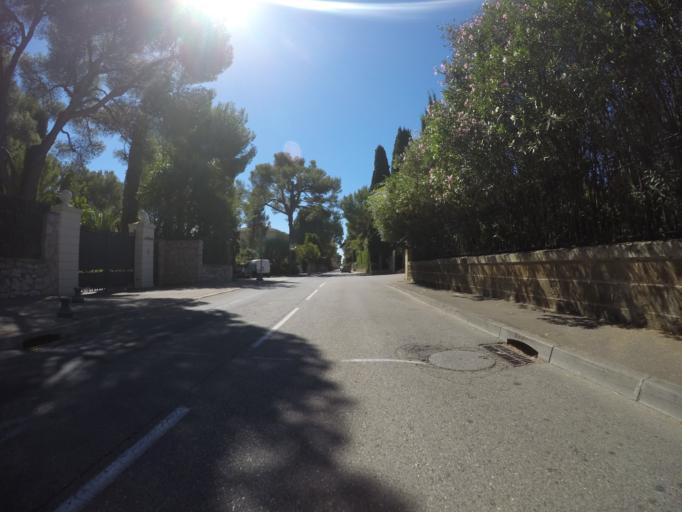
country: FR
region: Provence-Alpes-Cote d'Azur
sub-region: Departement des Alpes-Maritimes
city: Saint-Jean-Cap-Ferrat
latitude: 43.6868
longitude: 7.3306
